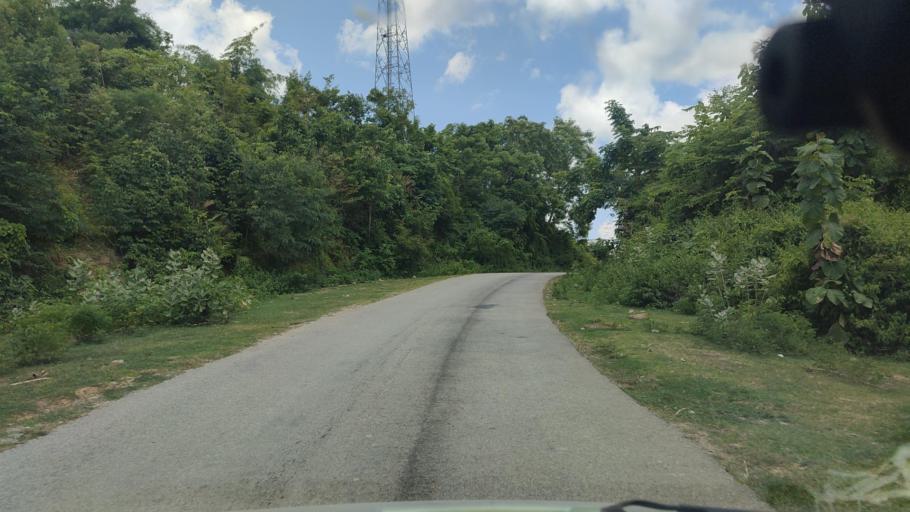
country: MM
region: Magway
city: Taungdwingyi
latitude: 20.0145
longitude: 95.8357
